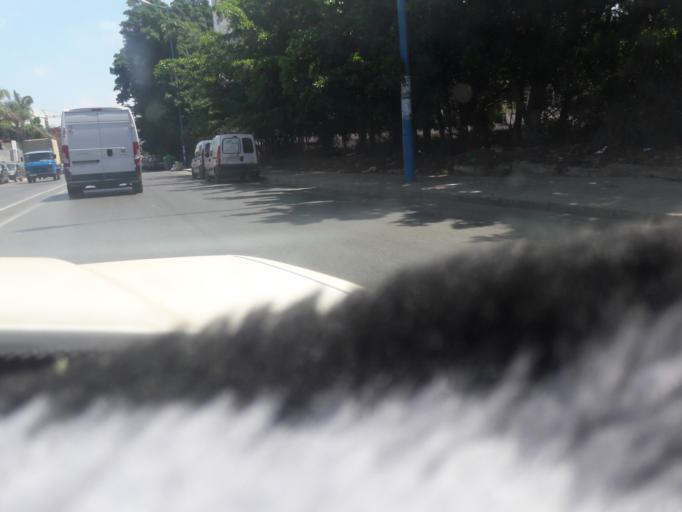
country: MA
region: Grand Casablanca
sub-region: Casablanca
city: Casablanca
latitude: 33.5761
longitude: -7.6607
